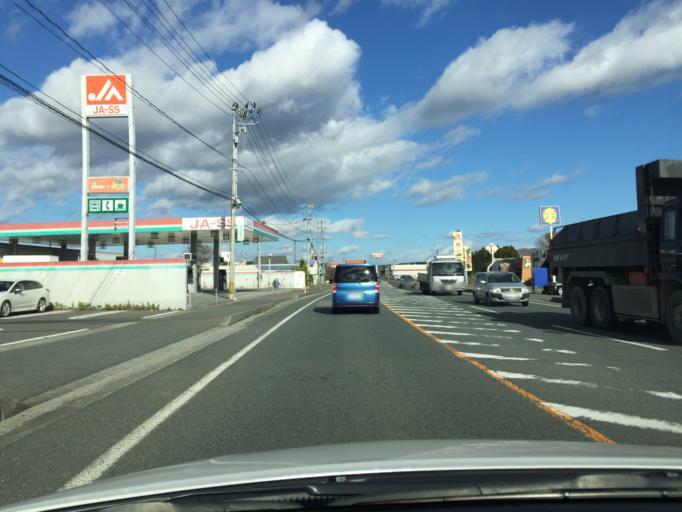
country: JP
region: Fukushima
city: Namie
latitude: 37.4850
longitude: 141.0054
